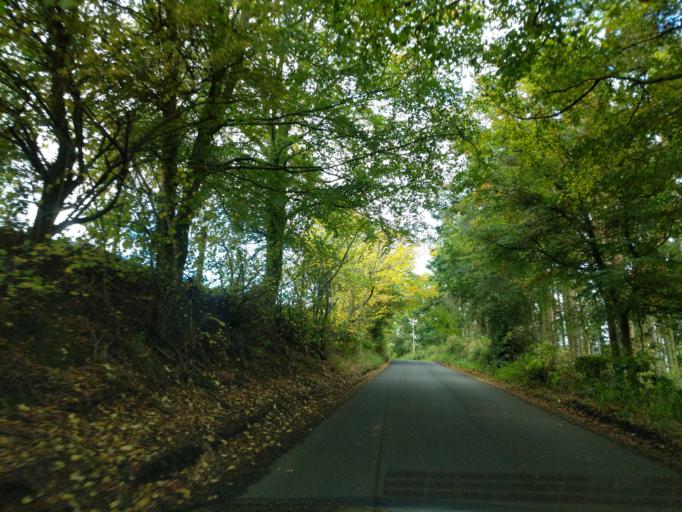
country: GB
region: Scotland
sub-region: East Lothian
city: Haddington
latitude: 55.9370
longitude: -2.7399
